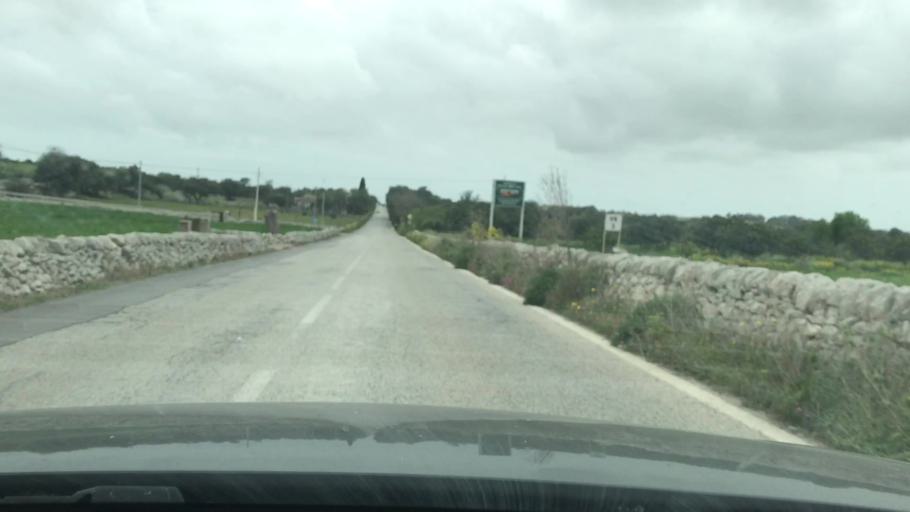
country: IT
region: Sicily
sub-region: Ragusa
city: Scicli
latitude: 36.8126
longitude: 14.7309
